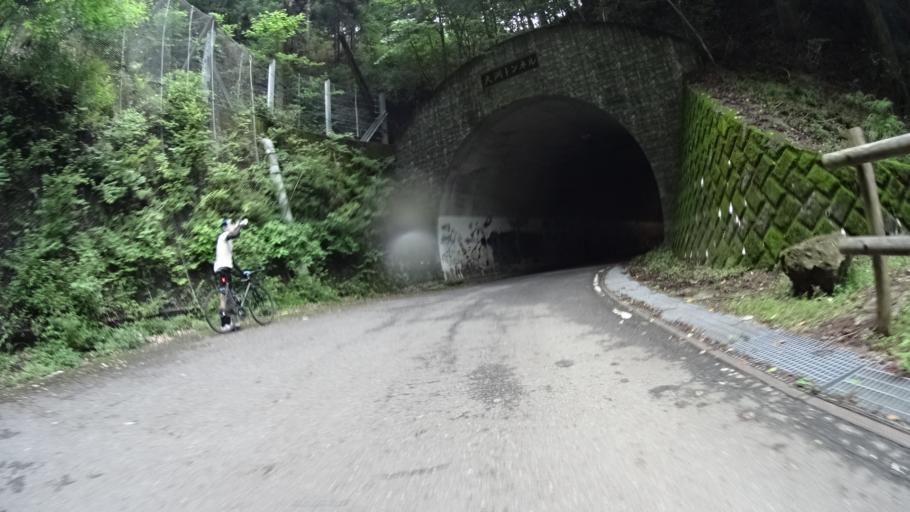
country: JP
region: Kanagawa
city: Hadano
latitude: 35.4759
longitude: 139.2104
